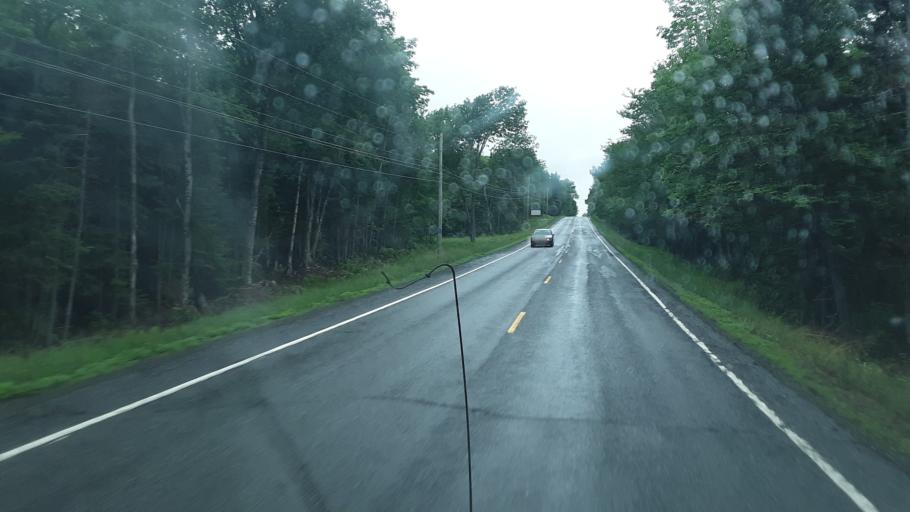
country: US
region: Maine
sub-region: Penobscot County
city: Patten
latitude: 46.1471
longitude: -68.3621
